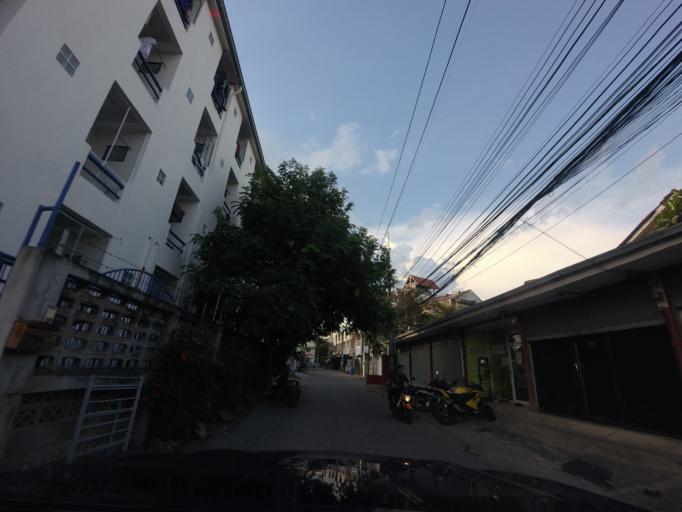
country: TH
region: Khon Kaen
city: Khon Kaen
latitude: 16.4252
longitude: 102.8611
